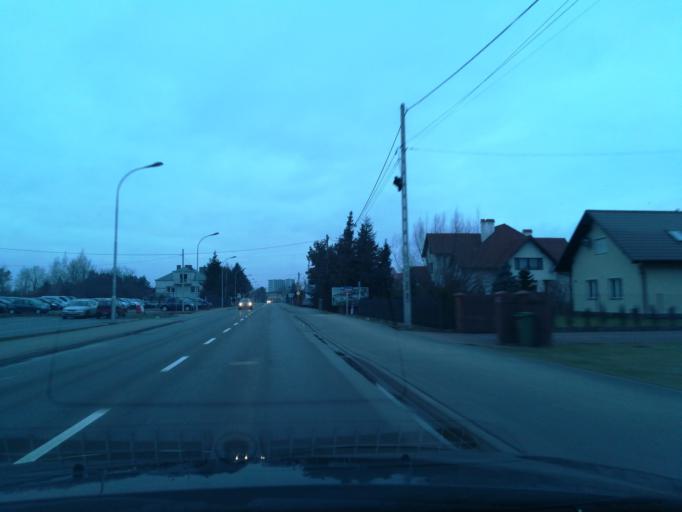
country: PL
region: Subcarpathian Voivodeship
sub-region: Rzeszow
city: Rzeszow
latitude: 50.0075
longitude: 22.0052
